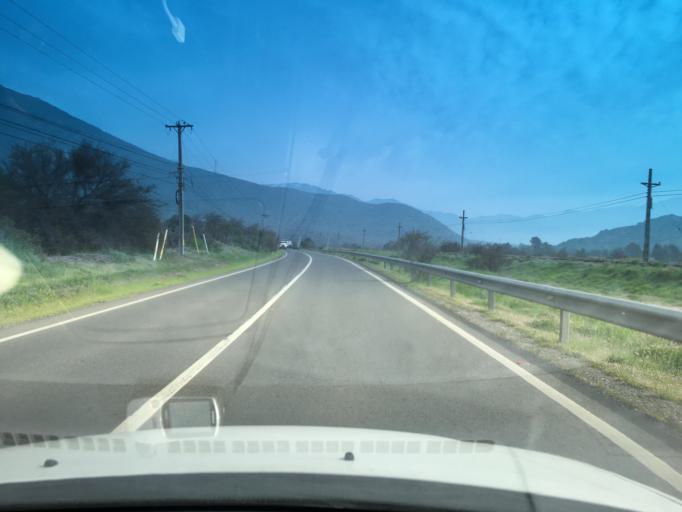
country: CL
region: Santiago Metropolitan
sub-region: Provincia de Chacabuco
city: Lampa
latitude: -33.1528
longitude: -70.9040
